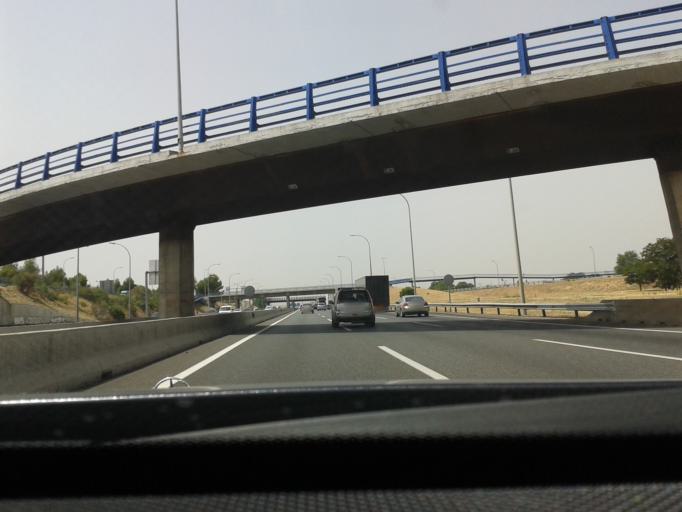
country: ES
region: Madrid
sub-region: Provincia de Madrid
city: Torrejon de Ardoz
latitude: 40.4651
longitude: -3.4819
